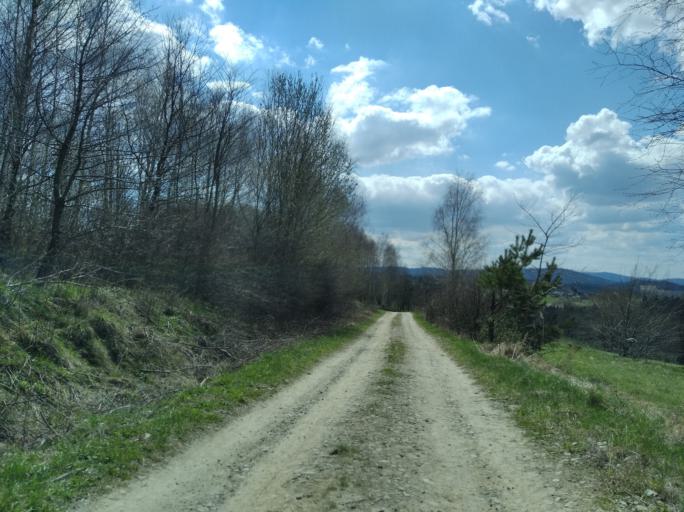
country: PL
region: Subcarpathian Voivodeship
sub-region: Powiat strzyzowski
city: Wysoka Strzyzowska
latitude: 49.8274
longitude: 21.7701
